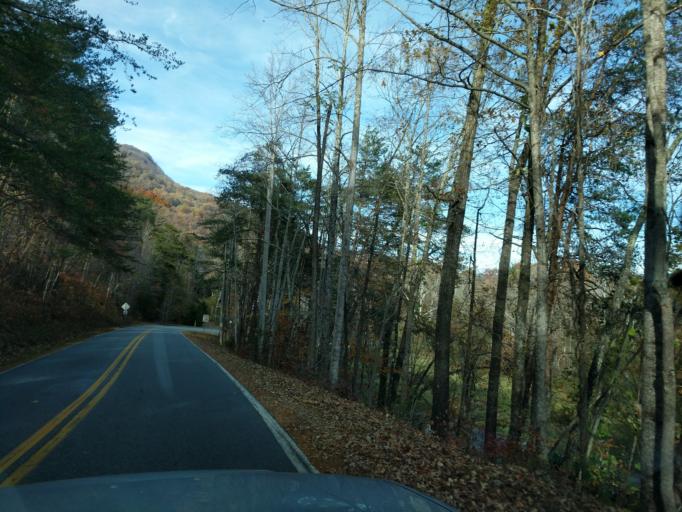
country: US
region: North Carolina
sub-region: Polk County
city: Columbus
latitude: 35.2583
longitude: -82.2137
